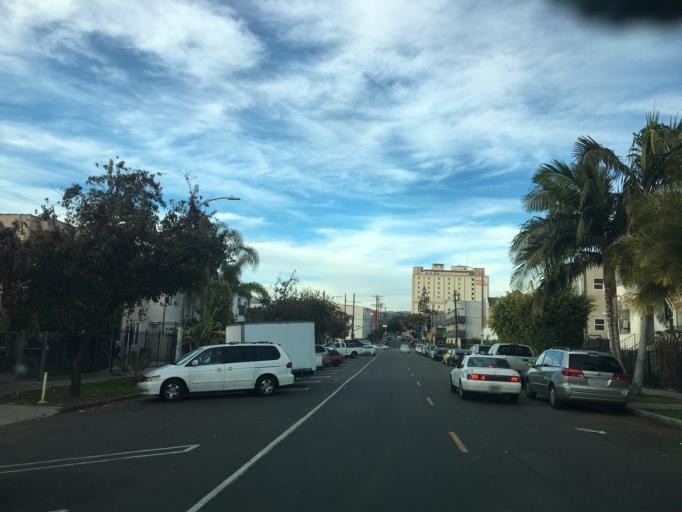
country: US
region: California
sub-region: Los Angeles County
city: Silver Lake
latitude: 34.0721
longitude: -118.2879
